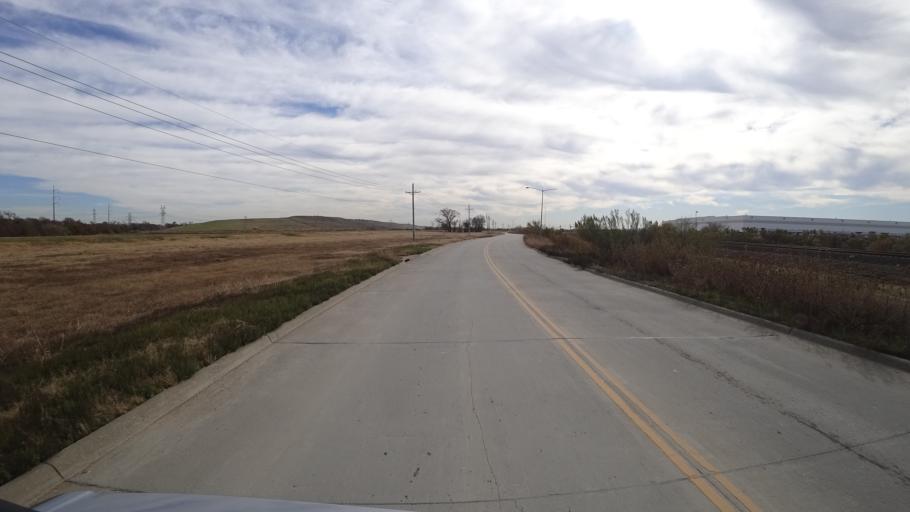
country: US
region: Texas
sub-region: Denton County
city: Lewisville
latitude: 33.0266
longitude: -96.9719
